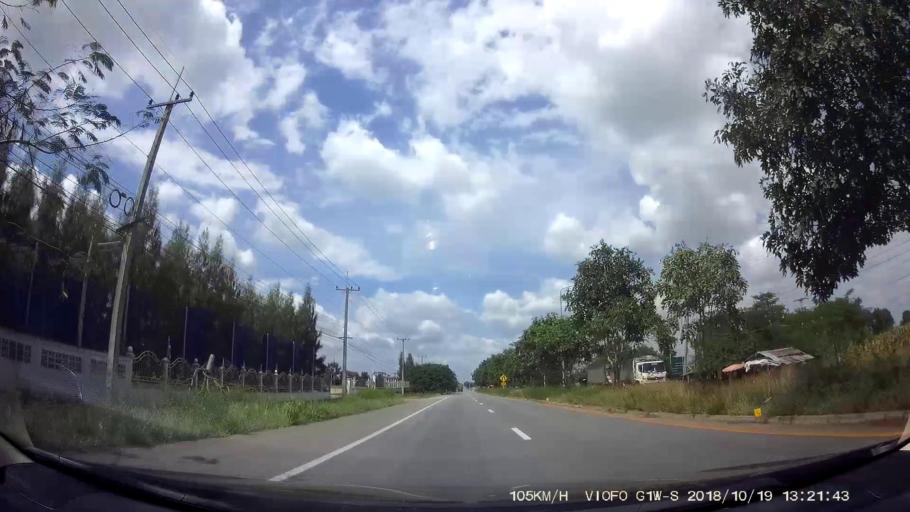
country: TH
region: Chaiyaphum
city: Chatturat
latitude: 15.4660
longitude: 101.8254
